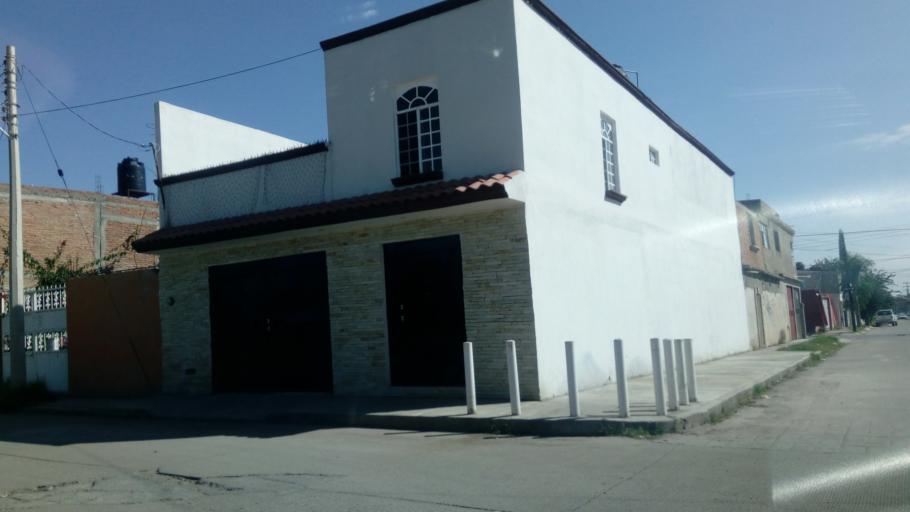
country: MX
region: Durango
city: Victoria de Durango
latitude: 24.0028
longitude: -104.6680
